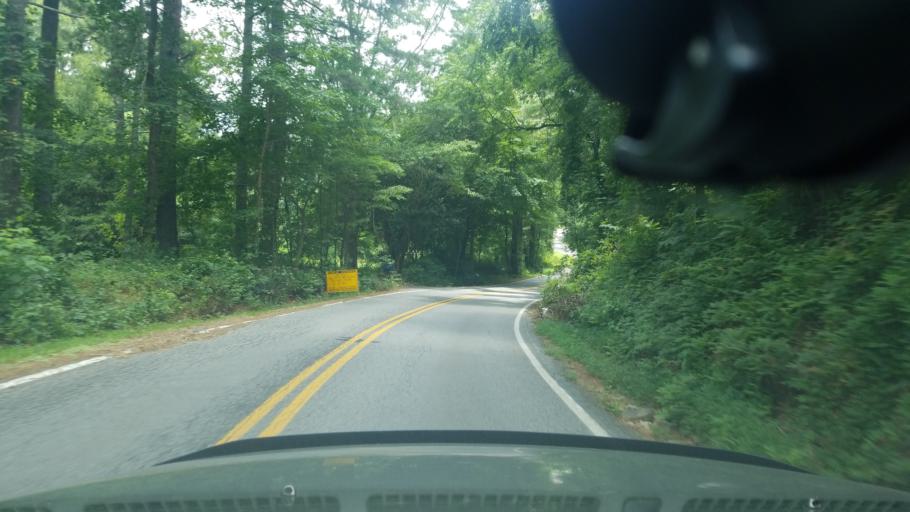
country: US
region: Georgia
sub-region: Fulton County
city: Milton
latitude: 34.1493
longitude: -84.2423
